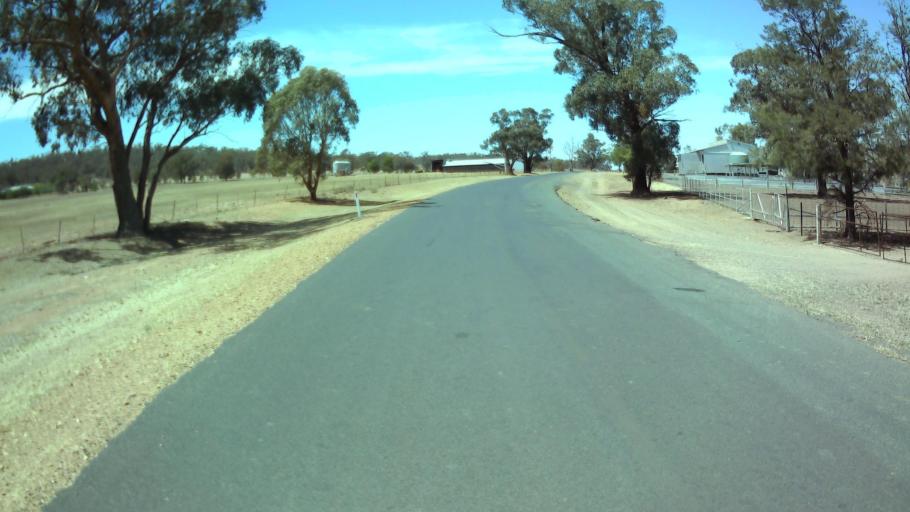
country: AU
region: New South Wales
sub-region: Weddin
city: Grenfell
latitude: -34.0997
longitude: 148.0070
